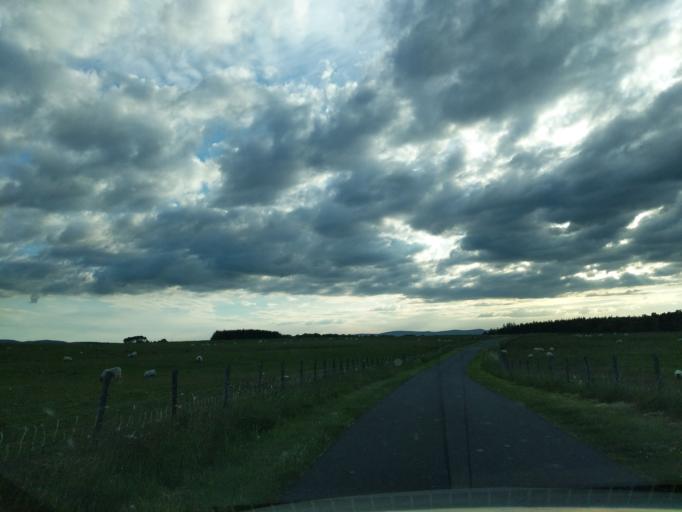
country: GB
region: Scotland
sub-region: Midlothian
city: Bonnyrigg
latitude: 55.7645
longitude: -3.1338
